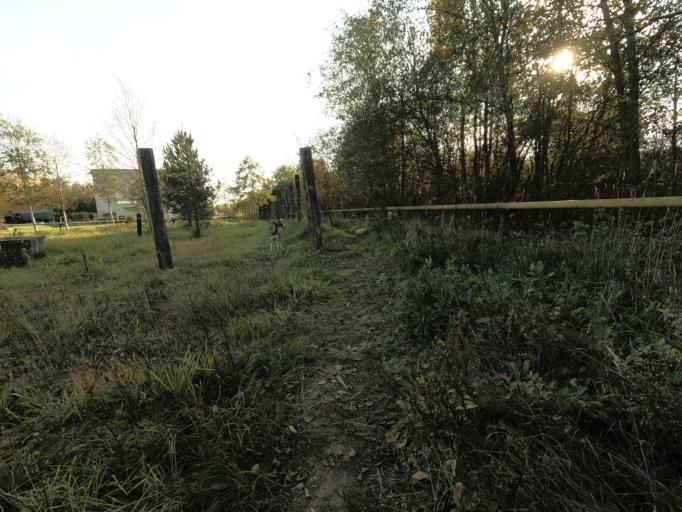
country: RU
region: Leningrad
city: Mga
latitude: 59.7443
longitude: 31.0610
